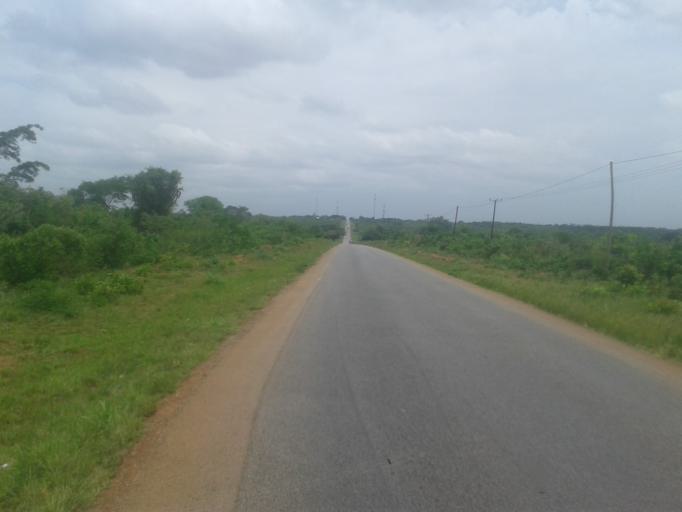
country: UG
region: Western Region
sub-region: Kiryandongo District
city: Masindi Port
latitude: 1.5016
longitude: 32.1197
